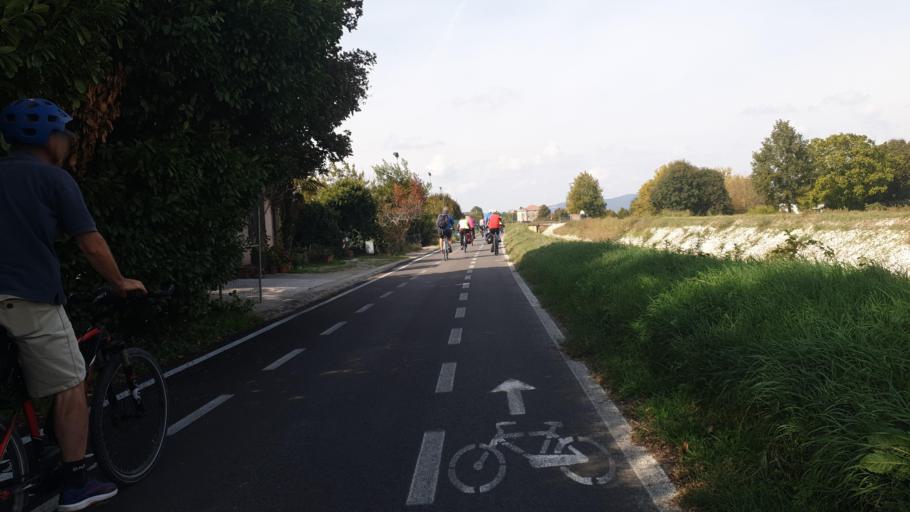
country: IT
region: Veneto
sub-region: Provincia di Vicenza
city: Agugliaro
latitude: 45.3257
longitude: 11.5872
